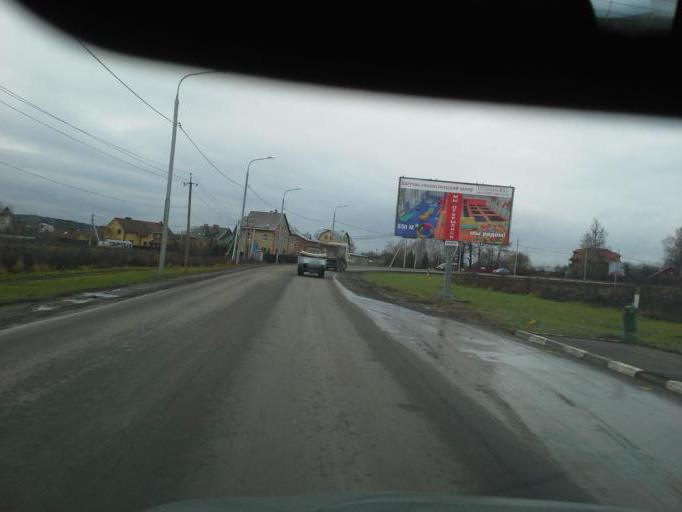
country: RU
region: Moskovskaya
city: Kommunarka
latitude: 55.5583
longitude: 37.4215
